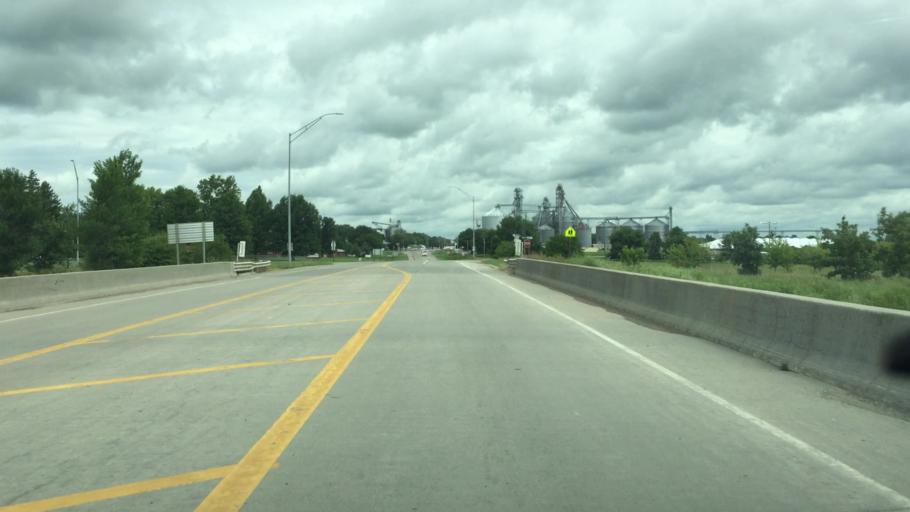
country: US
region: Iowa
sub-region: Jasper County
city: Monroe
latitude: 41.5113
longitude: -93.1012
